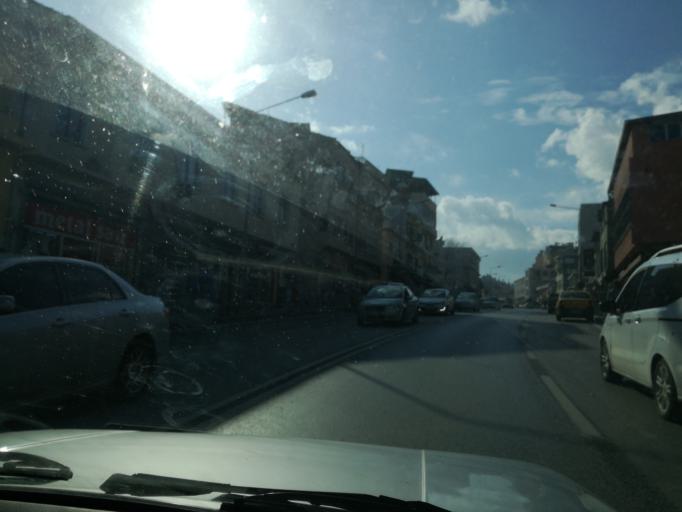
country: TR
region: Izmir
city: Izmir
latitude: 38.4178
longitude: 27.1367
